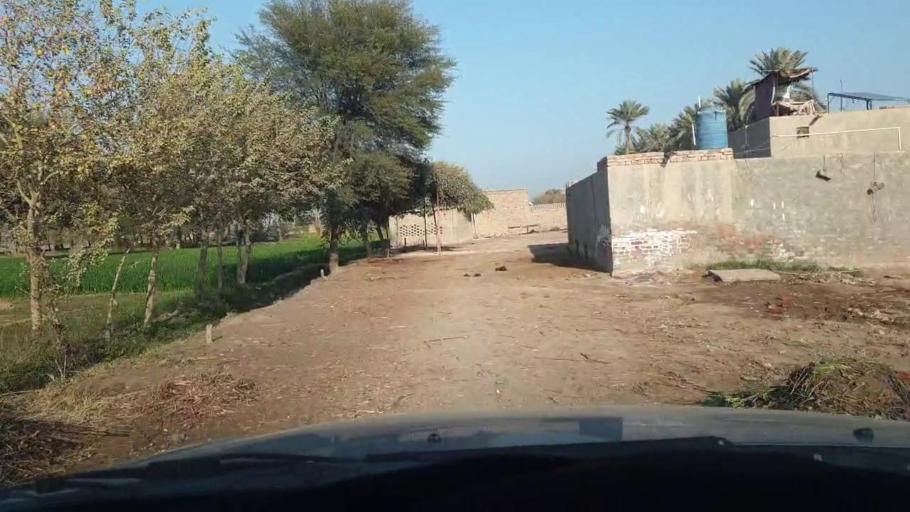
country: PK
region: Sindh
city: Mirpur Mathelo
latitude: 28.0250
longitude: 69.6039
